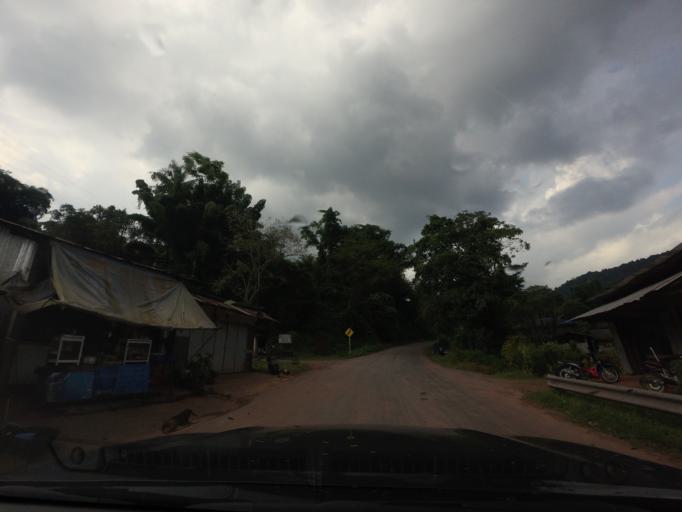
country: TH
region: Nan
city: Bo Kluea
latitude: 19.2704
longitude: 101.1779
